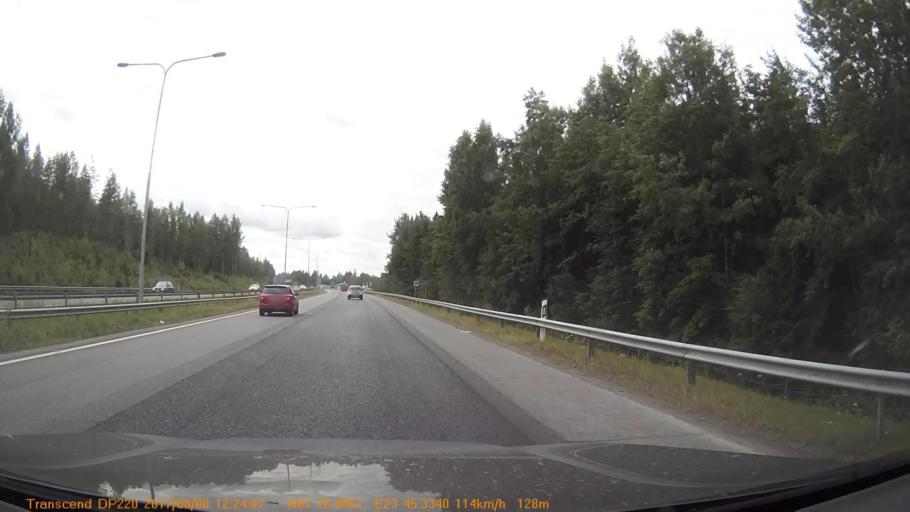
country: FI
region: Pirkanmaa
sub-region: Tampere
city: Tampere
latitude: 61.4331
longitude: 23.7555
